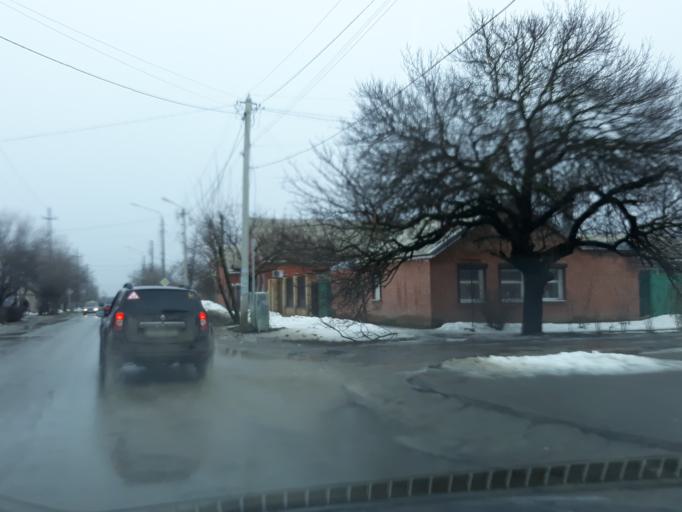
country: RU
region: Rostov
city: Taganrog
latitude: 47.2095
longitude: 38.8962
